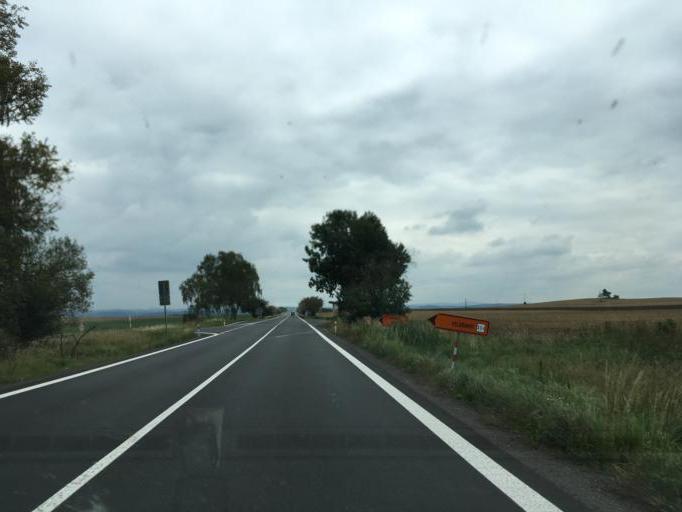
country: CZ
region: Vysocina
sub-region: Okres Pelhrimov
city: Zeliv
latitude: 49.5464
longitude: 15.1542
